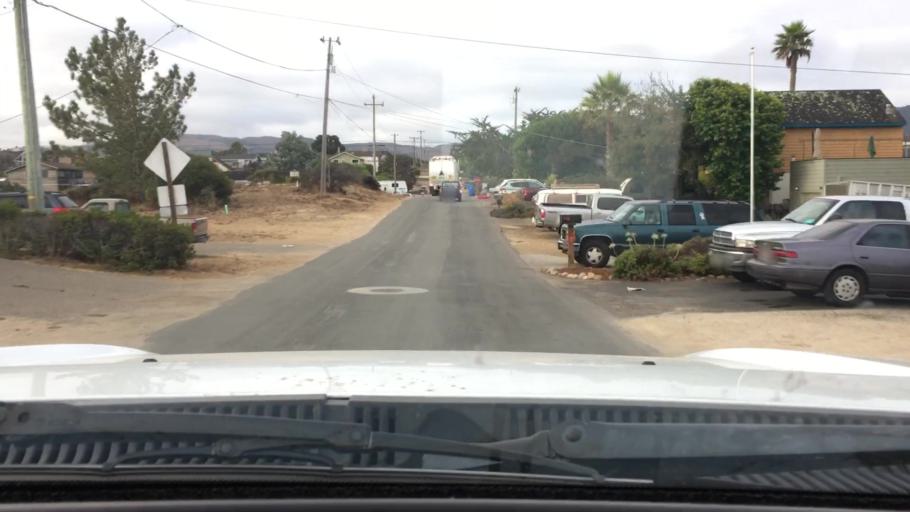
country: US
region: California
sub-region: San Luis Obispo County
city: Los Osos
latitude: 35.3255
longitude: -120.8288
